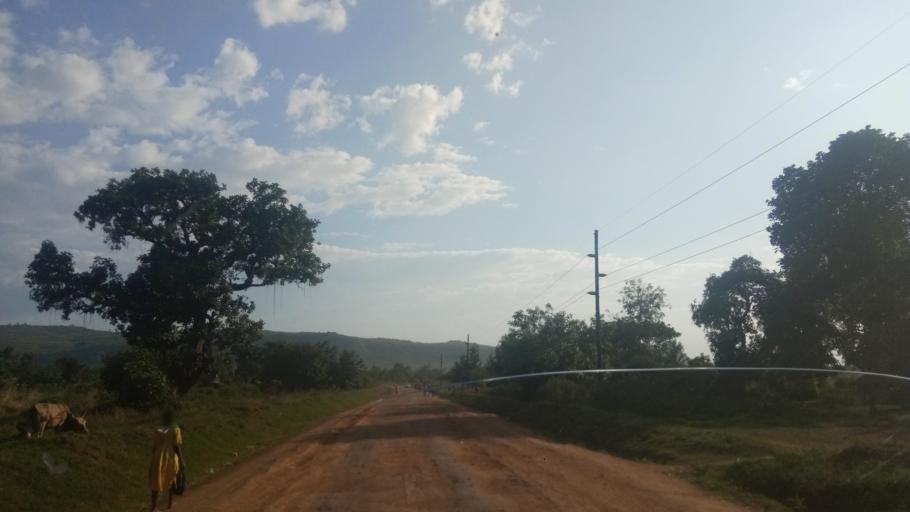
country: UG
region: Eastern Region
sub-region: Kapchorwa District
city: Kapchorwa
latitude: 1.4119
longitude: 34.3485
